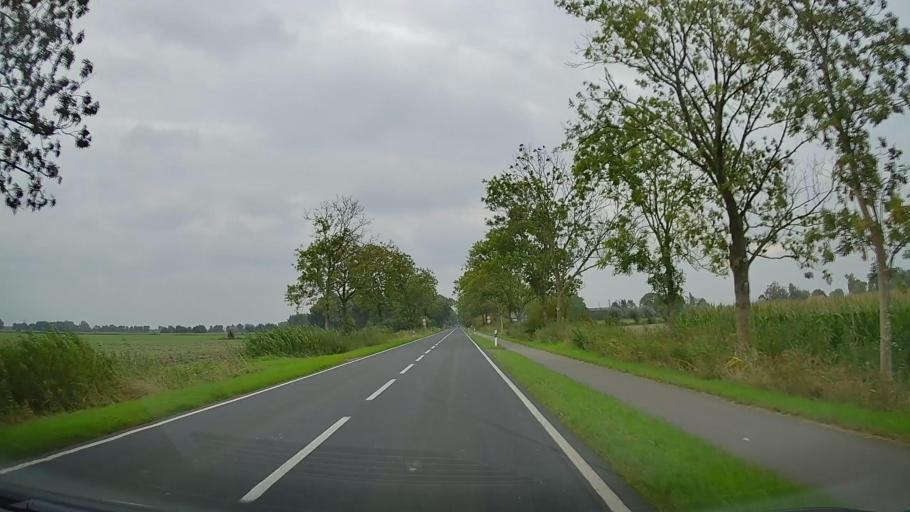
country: DE
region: Lower Saxony
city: Freiburg
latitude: 53.8143
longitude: 9.3008
